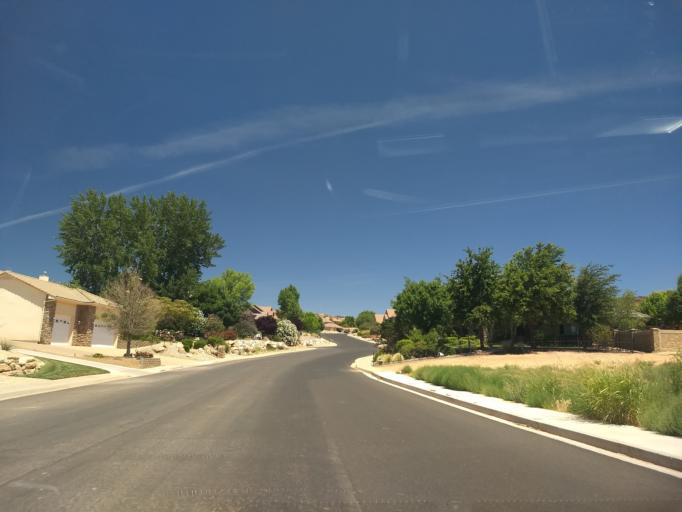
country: US
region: Utah
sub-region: Washington County
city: Washington
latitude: 37.0889
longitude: -113.4910
